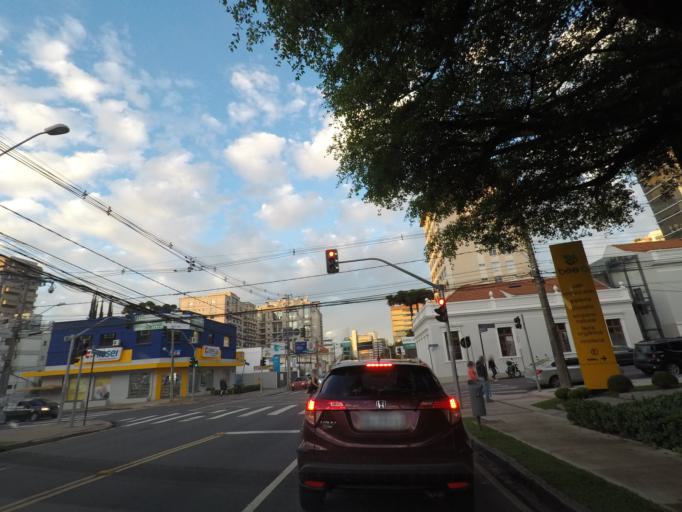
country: BR
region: Parana
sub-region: Curitiba
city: Curitiba
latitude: -25.4431
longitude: -49.2891
